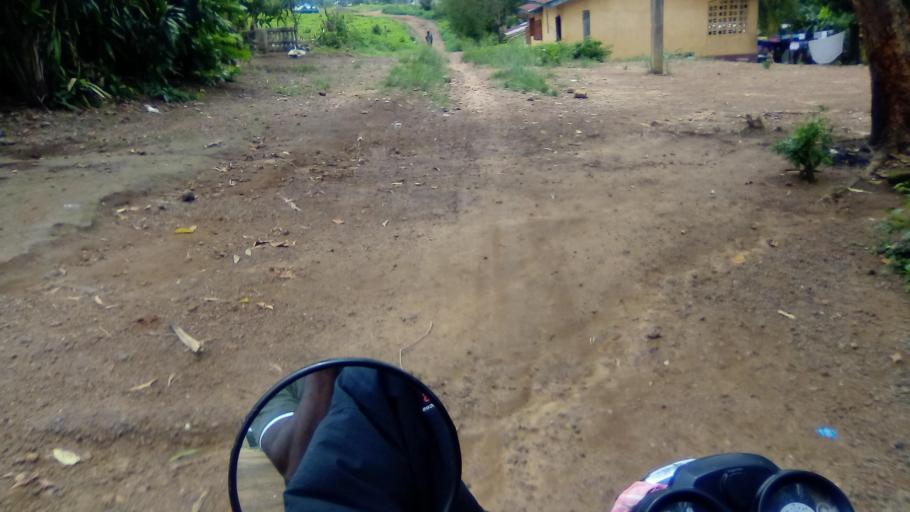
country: SL
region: Southern Province
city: Bo
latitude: 7.9337
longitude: -11.7198
